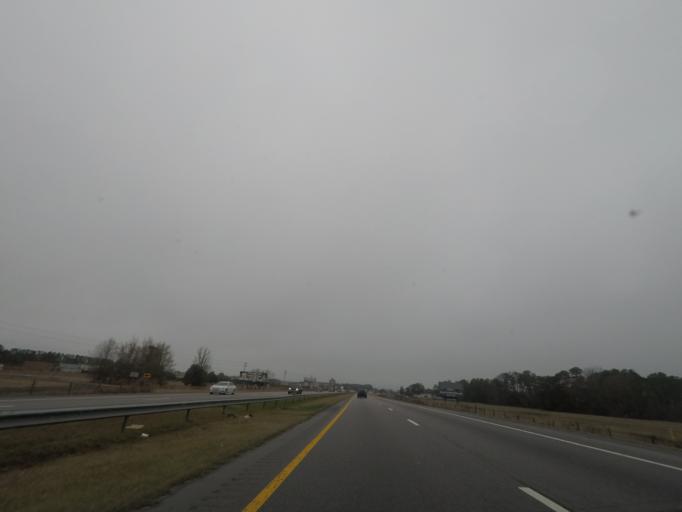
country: US
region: North Carolina
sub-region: Robeson County
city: Lumberton
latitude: 34.6197
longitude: -79.0628
